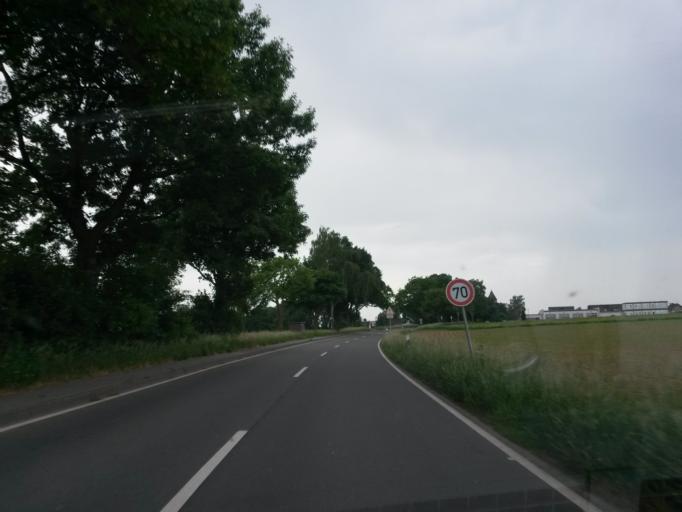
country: DE
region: North Rhine-Westphalia
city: Lohmar
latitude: 50.8768
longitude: 7.2297
